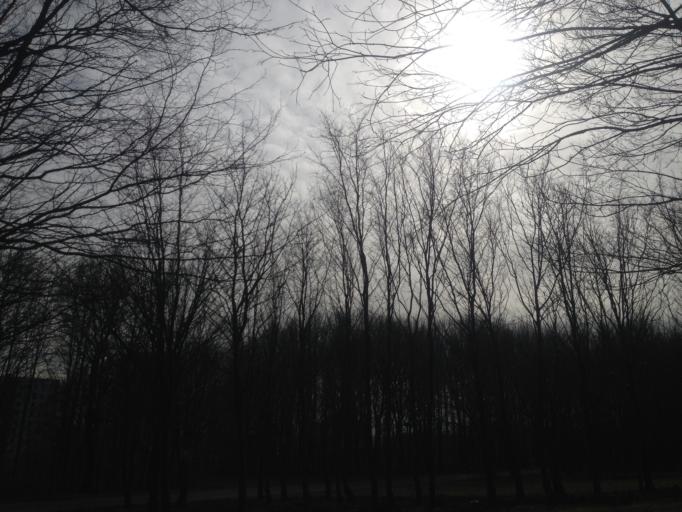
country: SE
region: Skane
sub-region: Lunds Kommun
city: Lund
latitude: 55.6967
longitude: 13.2435
